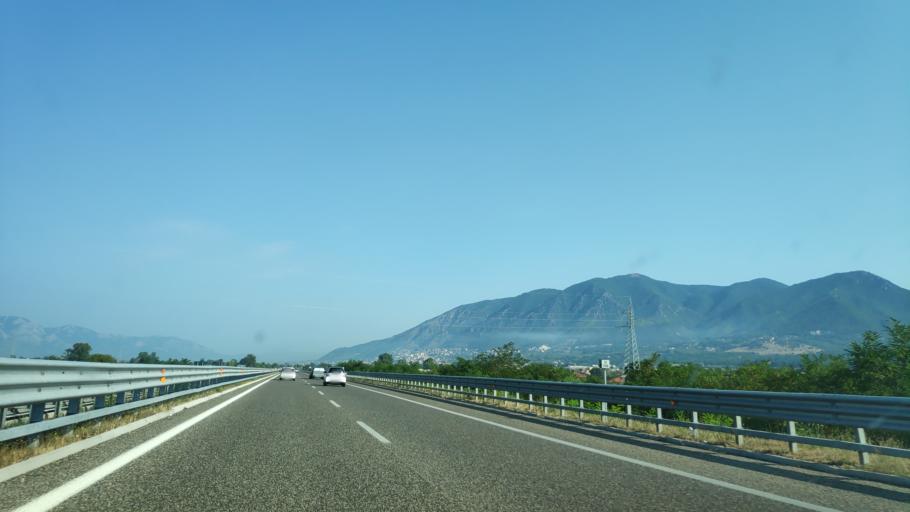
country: IT
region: Campania
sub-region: Provincia di Salerno
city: Padula
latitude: 40.3484
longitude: 15.6190
